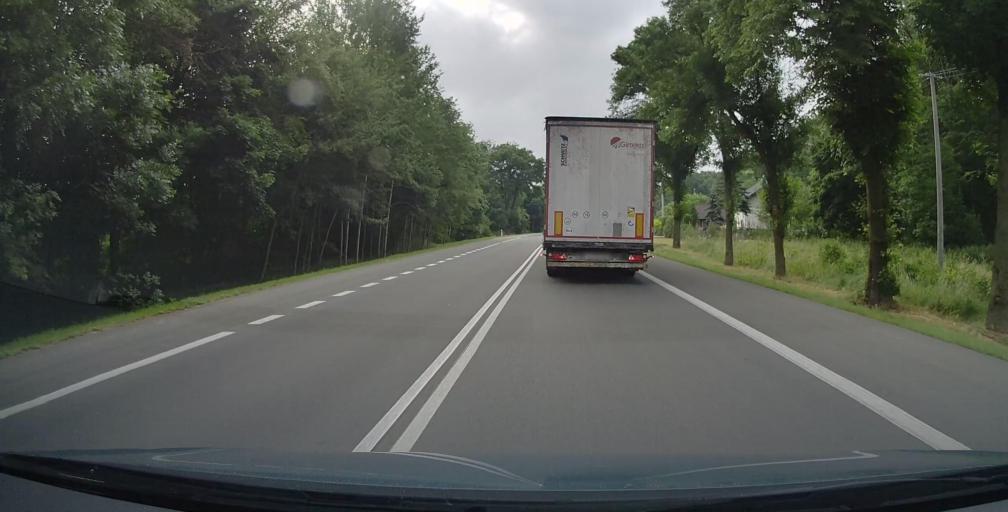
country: PL
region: Lublin Voivodeship
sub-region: Powiat lukowski
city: Trzebieszow
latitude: 52.0581
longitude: 22.6213
